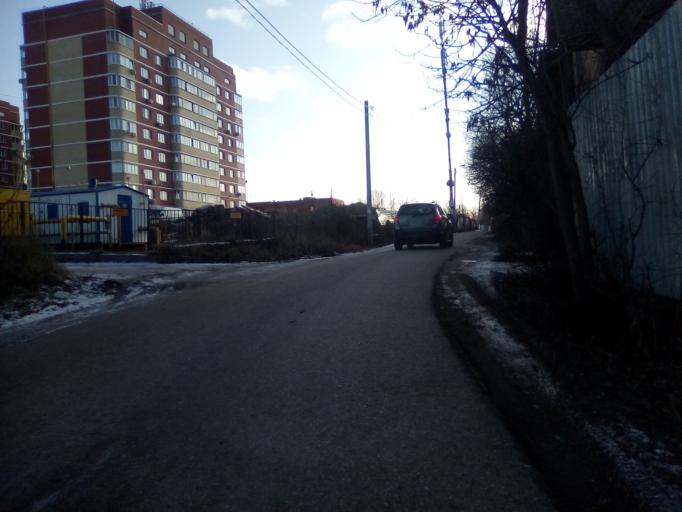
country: RU
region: Moskovskaya
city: Lesnoy Gorodok
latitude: 55.6686
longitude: 37.1789
